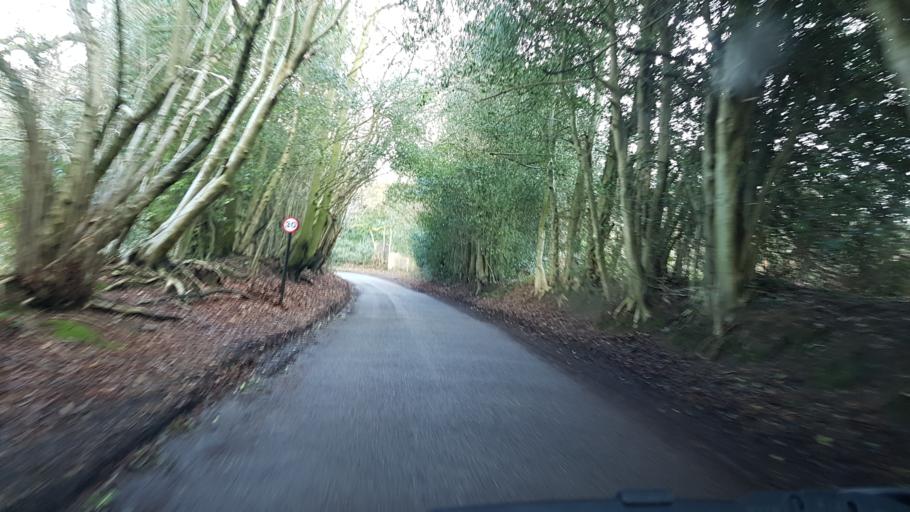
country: GB
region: England
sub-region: Surrey
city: Churt
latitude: 51.1161
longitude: -0.7768
